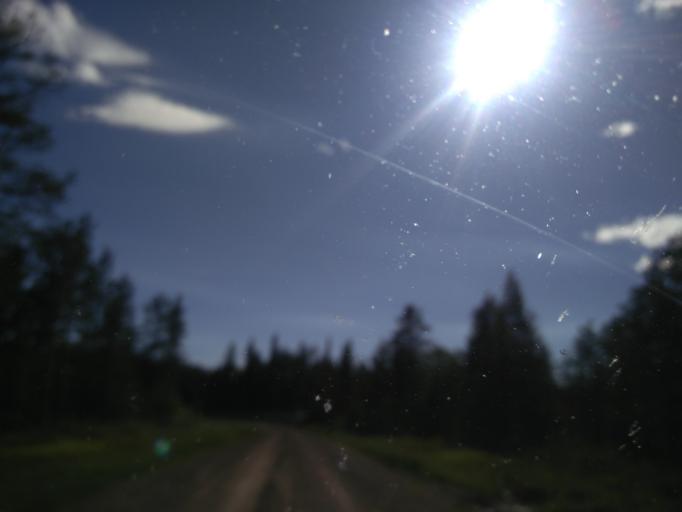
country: SE
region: Vaesternorrland
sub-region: Ange Kommun
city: Fransta
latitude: 62.2343
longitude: 16.3053
